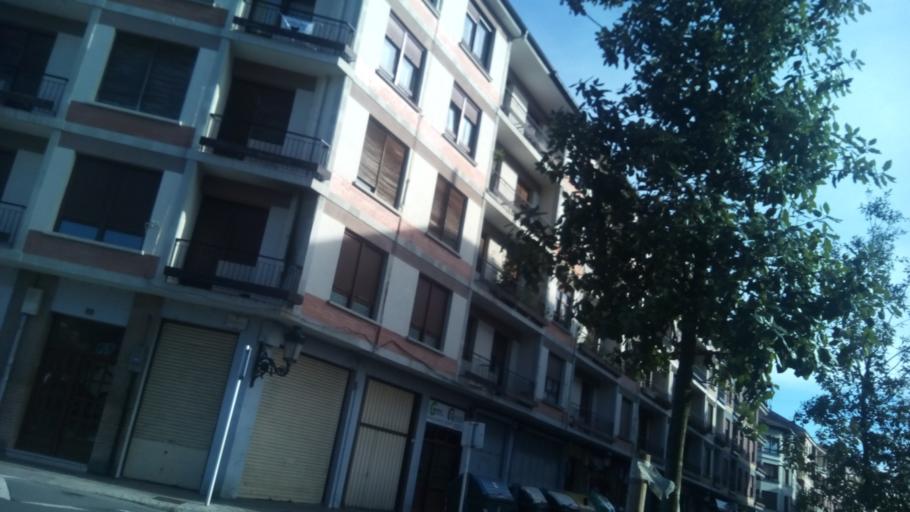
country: ES
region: Basque Country
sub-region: Bizkaia
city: Gernika-Lumo
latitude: 43.3177
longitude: -2.6770
